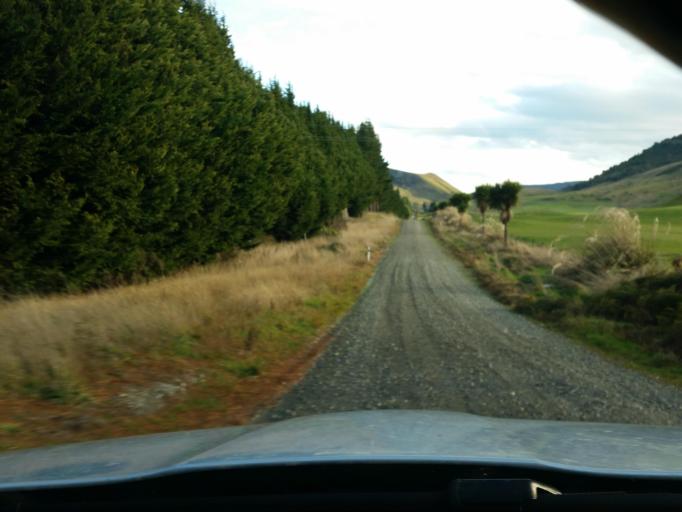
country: NZ
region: Southland
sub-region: Southland District
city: Te Anau
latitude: -45.8350
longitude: 167.6979
